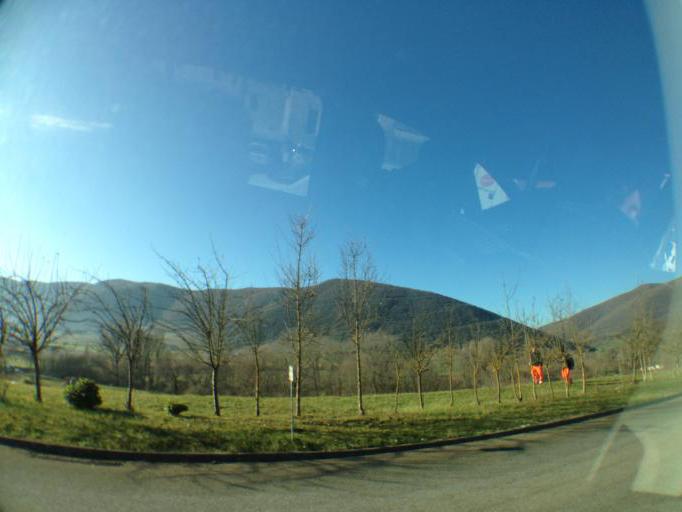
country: IT
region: Umbria
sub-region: Provincia di Perugia
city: Norcia
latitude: 42.7912
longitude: 13.0919
